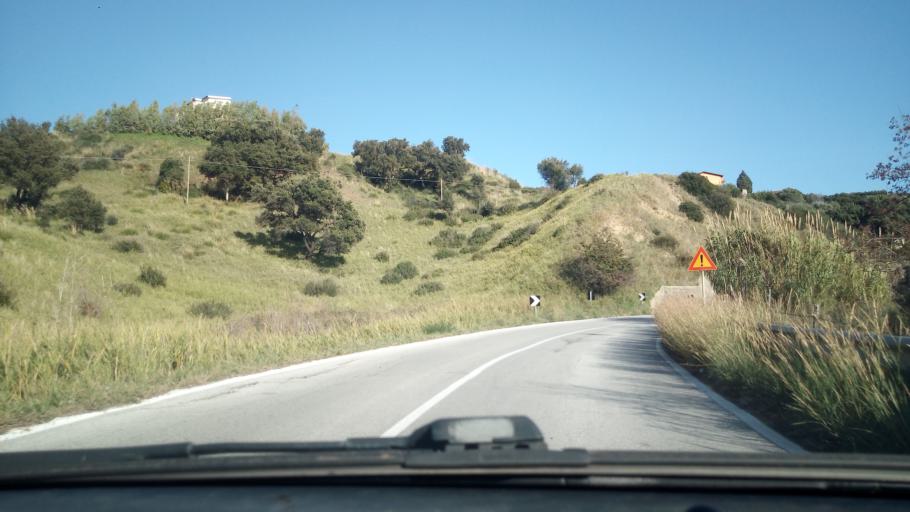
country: IT
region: Calabria
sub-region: Provincia di Catanzaro
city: Roccelletta
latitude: 38.8308
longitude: 16.5957
